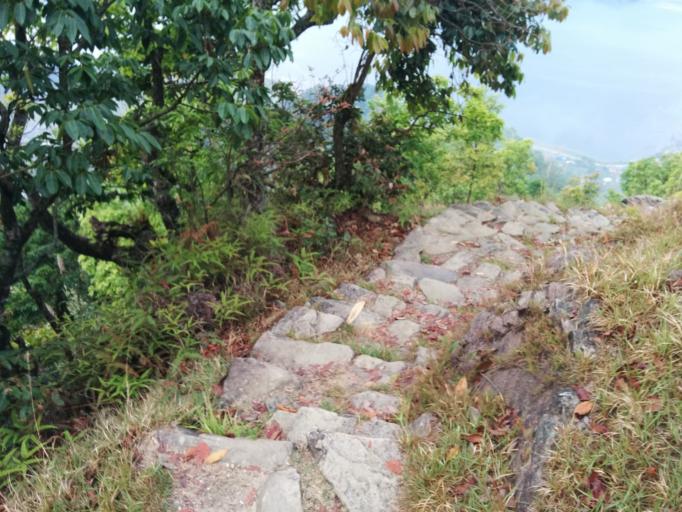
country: NP
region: Western Region
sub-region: Gandaki Zone
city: Pokhara
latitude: 28.2346
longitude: 83.9476
